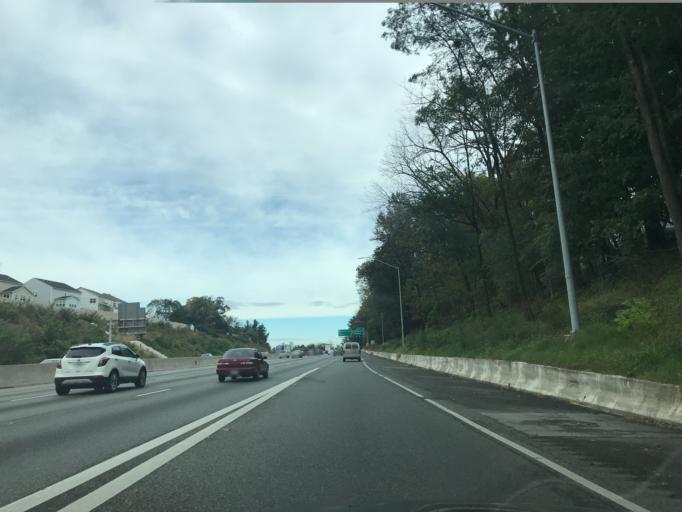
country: US
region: Maryland
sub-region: Baltimore County
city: Catonsville
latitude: 39.2751
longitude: -76.7246
